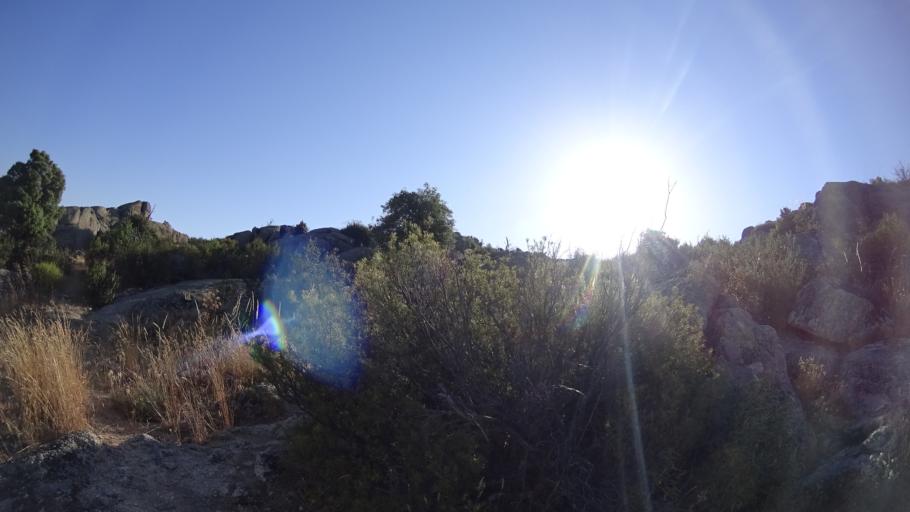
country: ES
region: Madrid
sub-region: Provincia de Madrid
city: Moralzarzal
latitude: 40.6490
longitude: -3.9547
